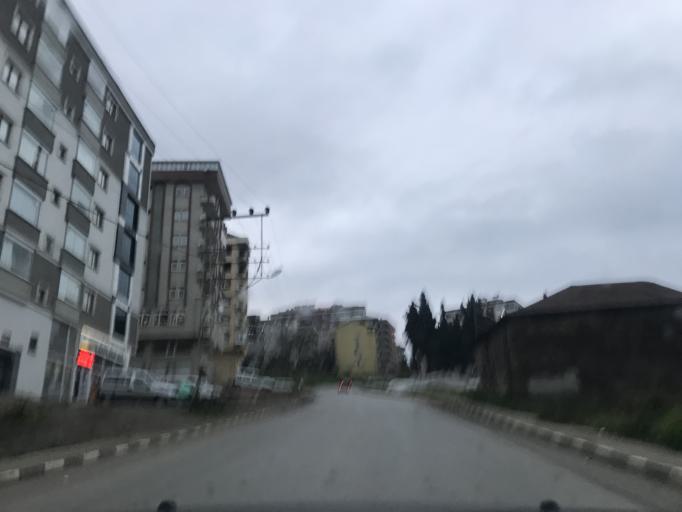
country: TR
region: Trabzon
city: Akcaabat
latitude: 41.0115
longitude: 39.5905
